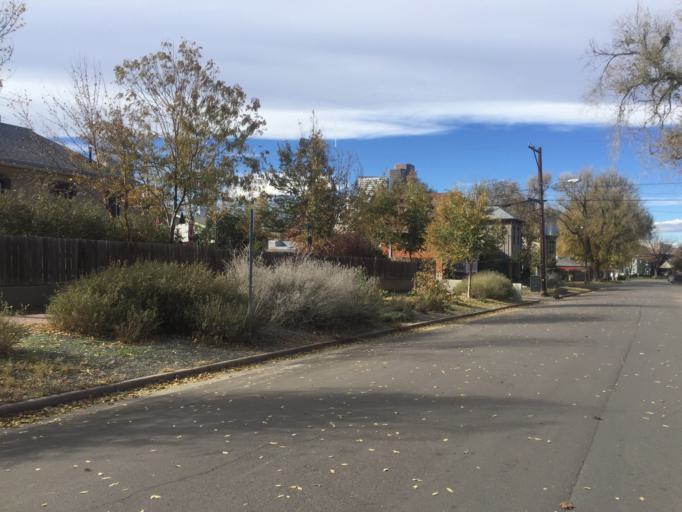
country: US
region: Colorado
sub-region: Denver County
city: Denver
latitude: 39.7520
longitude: -104.9759
